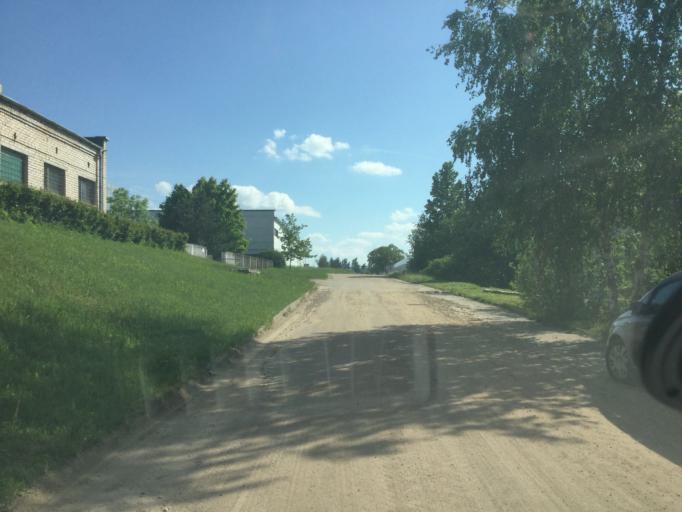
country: BY
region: Vitebsk
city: Vitebsk
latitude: 55.1673
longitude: 30.2433
